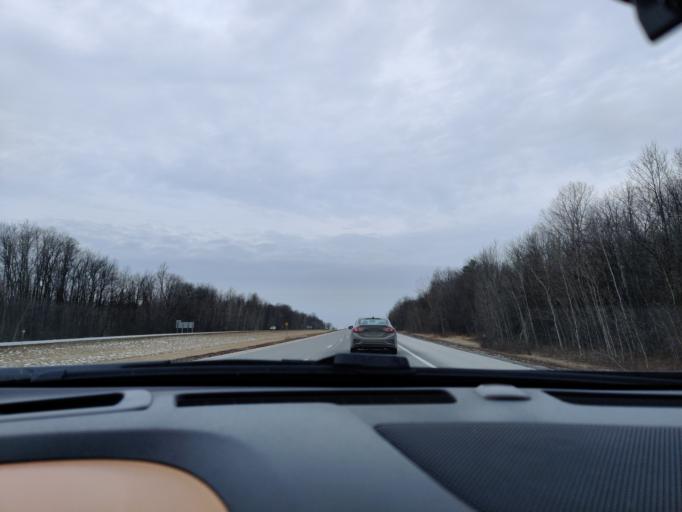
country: US
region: New York
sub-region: St. Lawrence County
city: Norfolk
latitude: 44.9085
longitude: -75.2188
